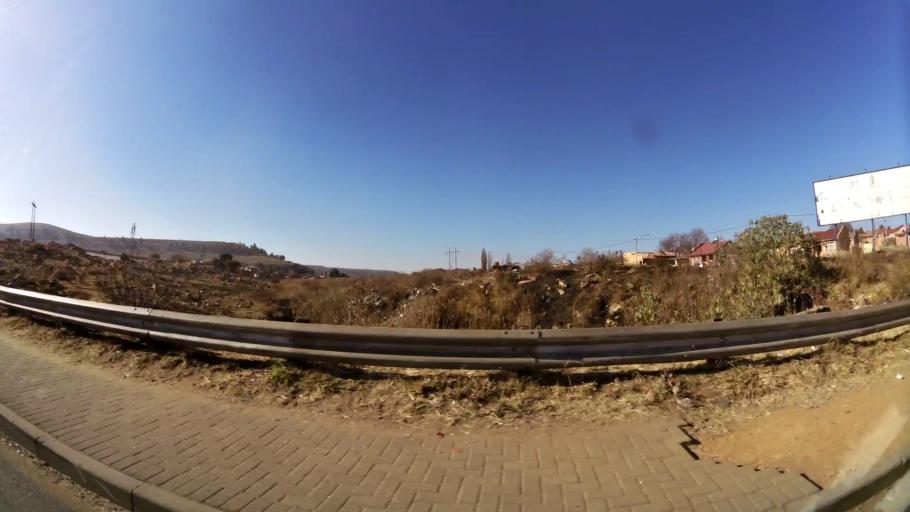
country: ZA
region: Gauteng
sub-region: City of Johannesburg Metropolitan Municipality
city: Soweto
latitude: -26.2254
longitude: 27.9379
